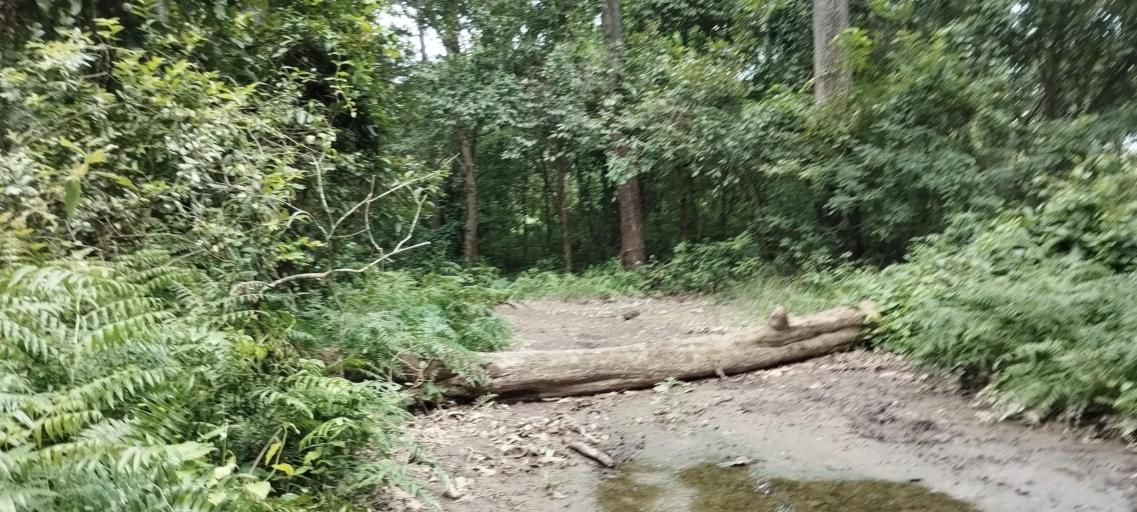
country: NP
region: Far Western
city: Tikapur
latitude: 28.4851
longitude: 81.2513
